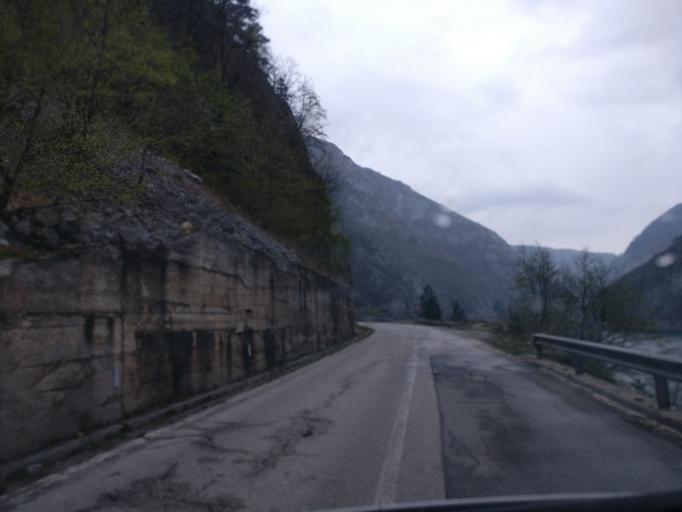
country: ME
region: Opstina Pluzine
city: Pluzine
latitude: 43.2444
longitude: 18.8359
